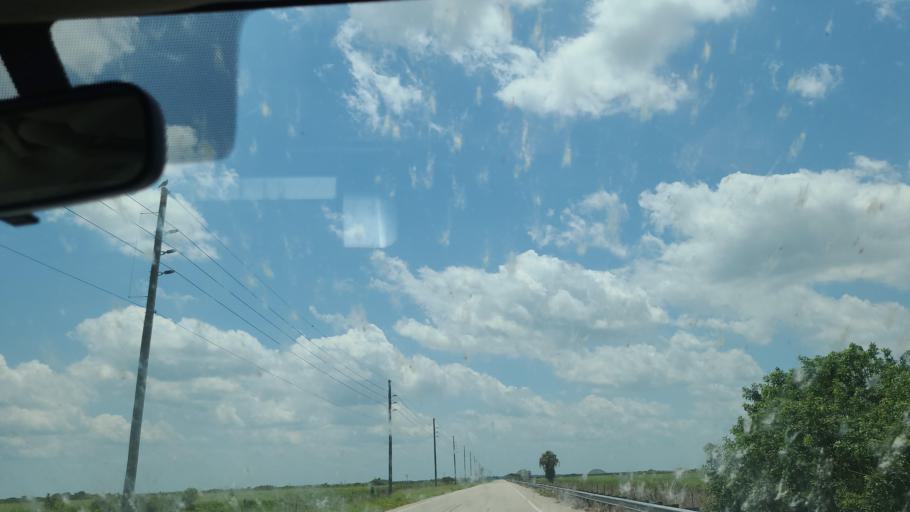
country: US
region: Florida
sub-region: Glades County
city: Buckhead Ridge
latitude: 27.1786
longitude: -81.0940
